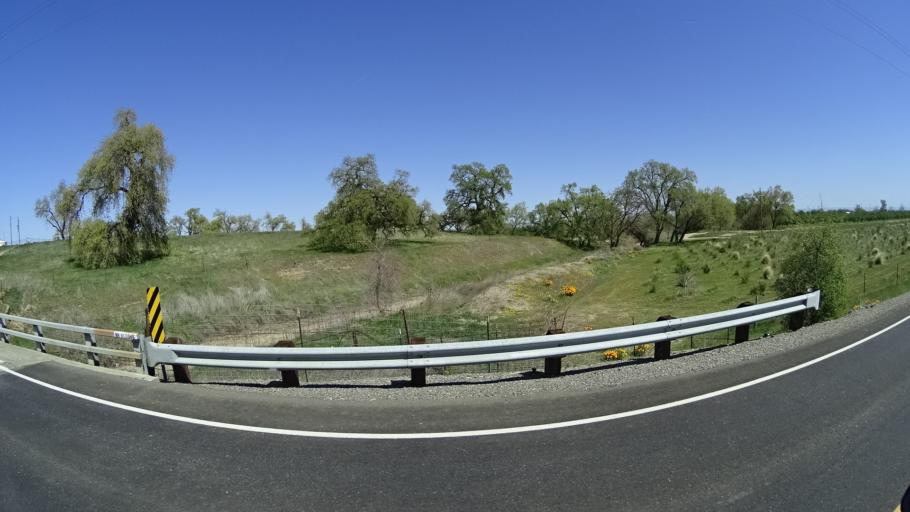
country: US
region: California
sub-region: Glenn County
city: Orland
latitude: 39.7817
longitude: -122.2940
